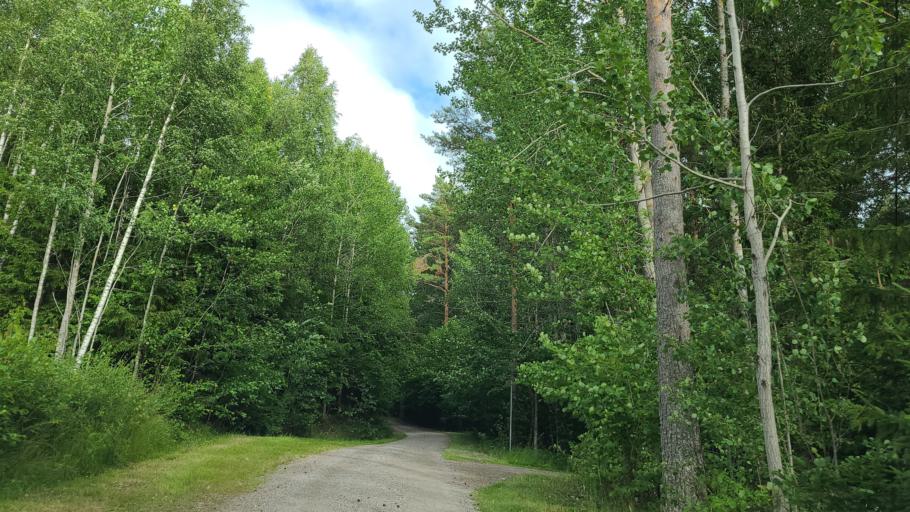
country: FI
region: Varsinais-Suomi
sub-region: Aboland-Turunmaa
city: Nagu
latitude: 60.1295
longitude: 21.8071
